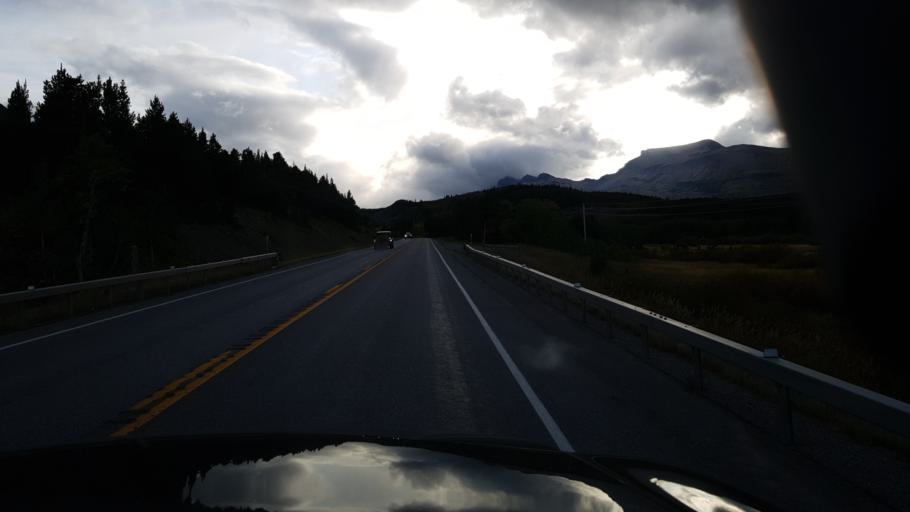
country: US
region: Montana
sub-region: Glacier County
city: South Browning
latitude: 48.4052
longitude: -113.2446
